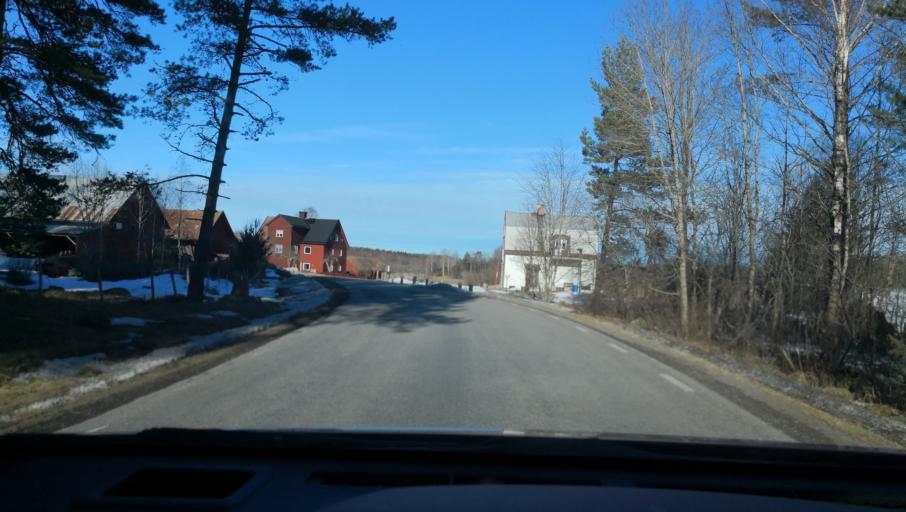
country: SE
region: Uppsala
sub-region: Osthammars Kommun
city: Osterbybruk
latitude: 60.2346
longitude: 17.9219
